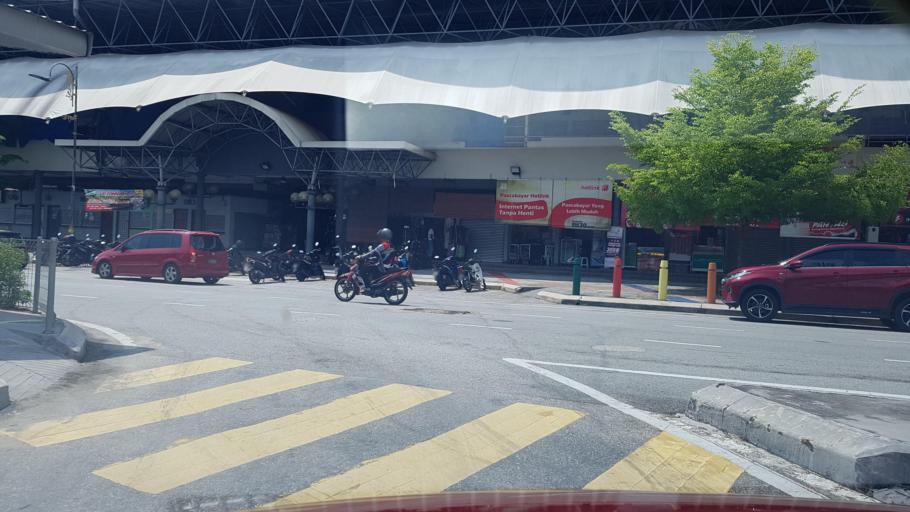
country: MY
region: Terengganu
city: Kuala Terengganu
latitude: 5.3326
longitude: 103.1366
